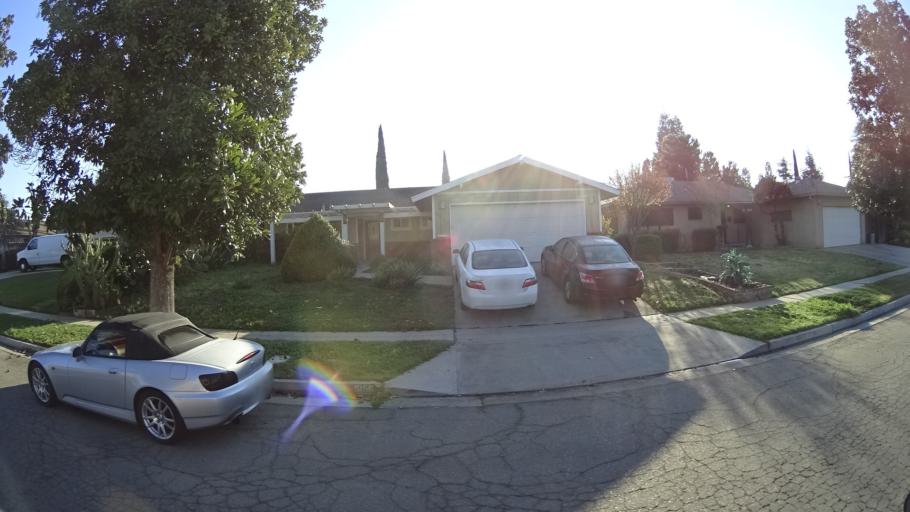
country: US
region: California
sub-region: Fresno County
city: Fresno
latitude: 36.8114
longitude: -119.7734
